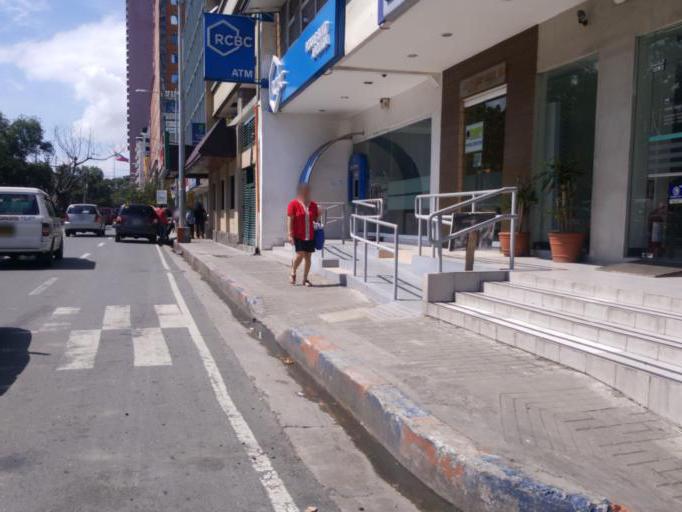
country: PH
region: Metro Manila
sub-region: City of Manila
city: Port Area
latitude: 14.5773
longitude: 120.9791
